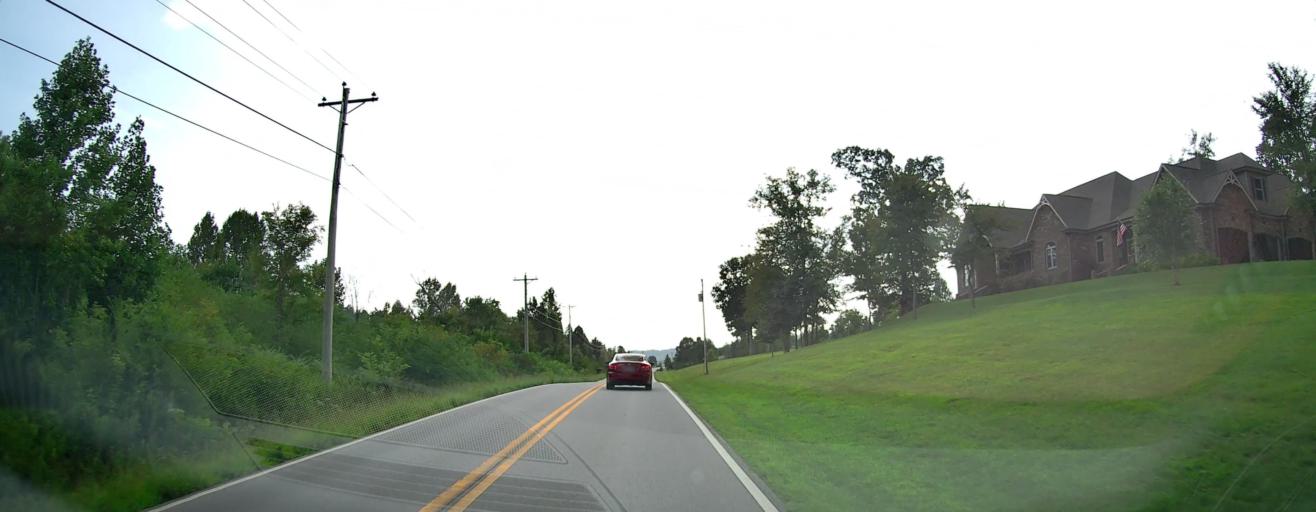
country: US
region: Georgia
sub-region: Catoosa County
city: Ringgold
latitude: 34.9582
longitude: -85.0718
